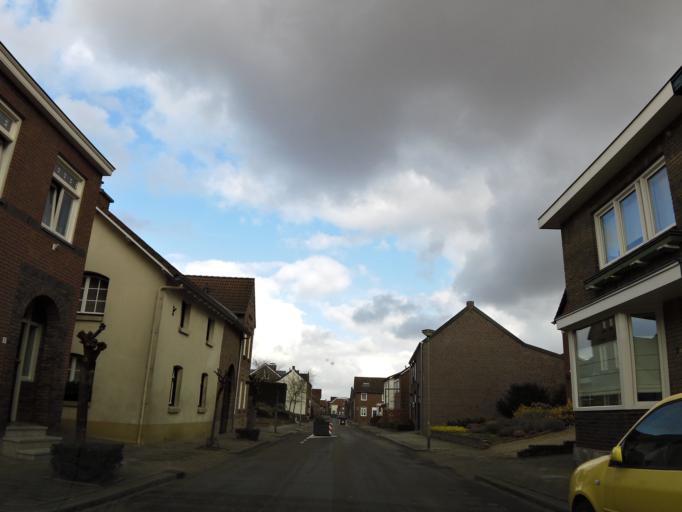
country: NL
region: Limburg
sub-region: Gemeente Stein
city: Berg
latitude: 51.0004
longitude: 5.7699
